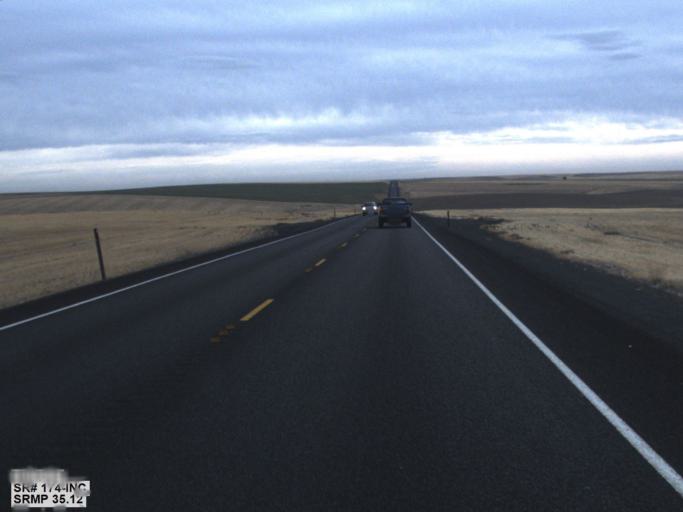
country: US
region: Washington
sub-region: Okanogan County
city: Coulee Dam
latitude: 47.8341
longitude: -118.7958
